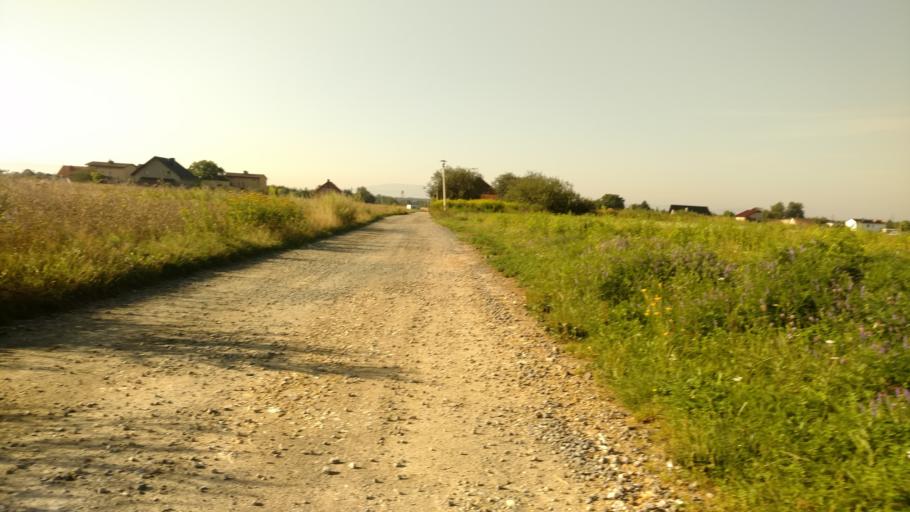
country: PL
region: Silesian Voivodeship
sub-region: Powiat pszczynski
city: Pszczyna
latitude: 49.9917
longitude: 18.9673
